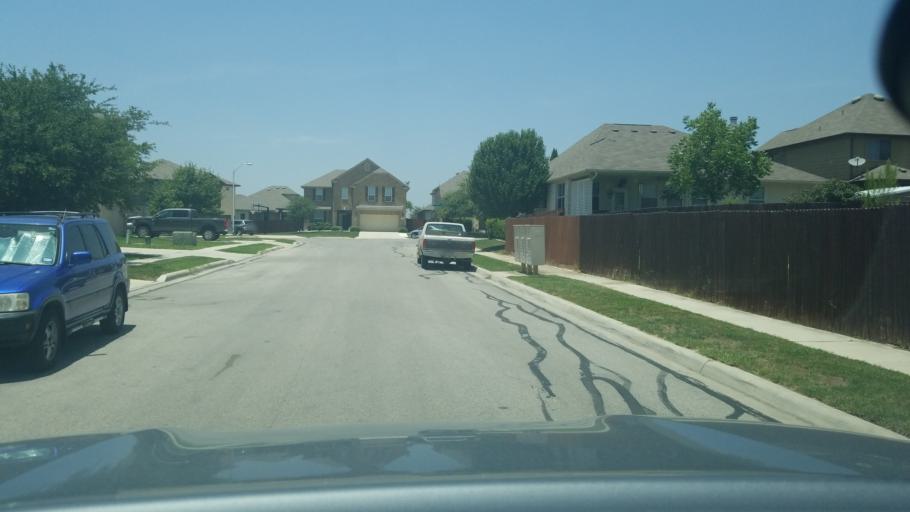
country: US
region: Texas
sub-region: Guadalupe County
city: Cibolo
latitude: 29.5795
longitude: -98.2297
